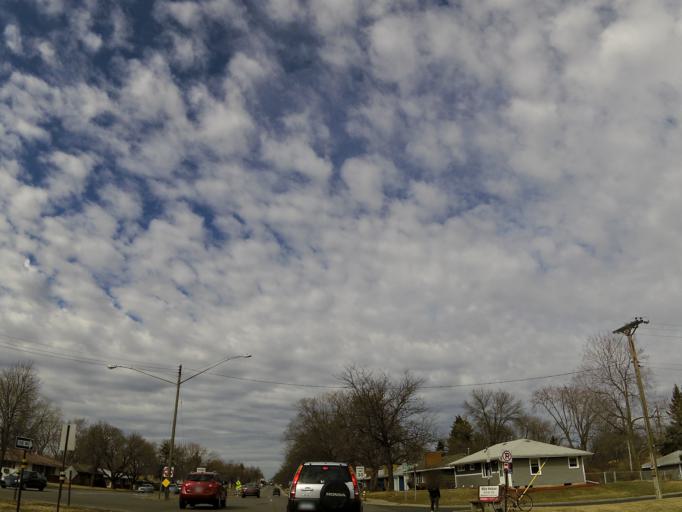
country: US
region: Minnesota
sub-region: Hennepin County
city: Edina
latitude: 44.8850
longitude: -93.3189
